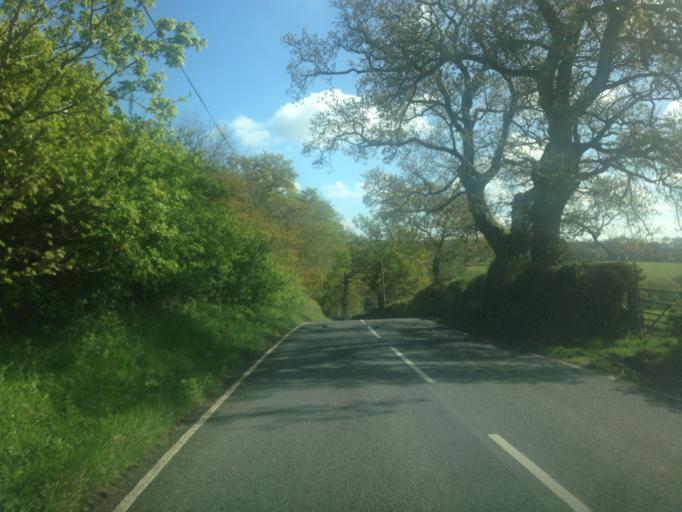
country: GB
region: Wales
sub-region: County of Ceredigion
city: Newcastle Emlyn
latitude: 52.0486
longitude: -4.4627
